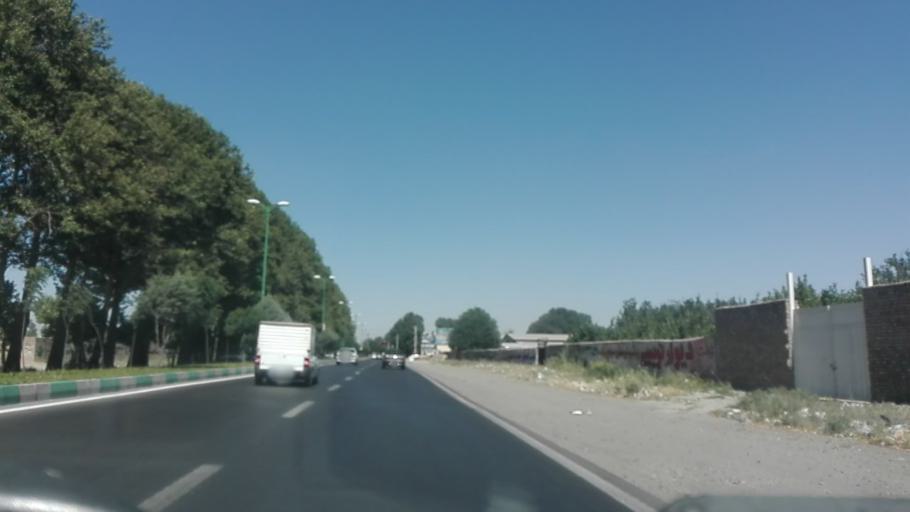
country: IR
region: Tehran
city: Shahre Jadide Andisheh
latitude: 35.6541
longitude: 51.0292
